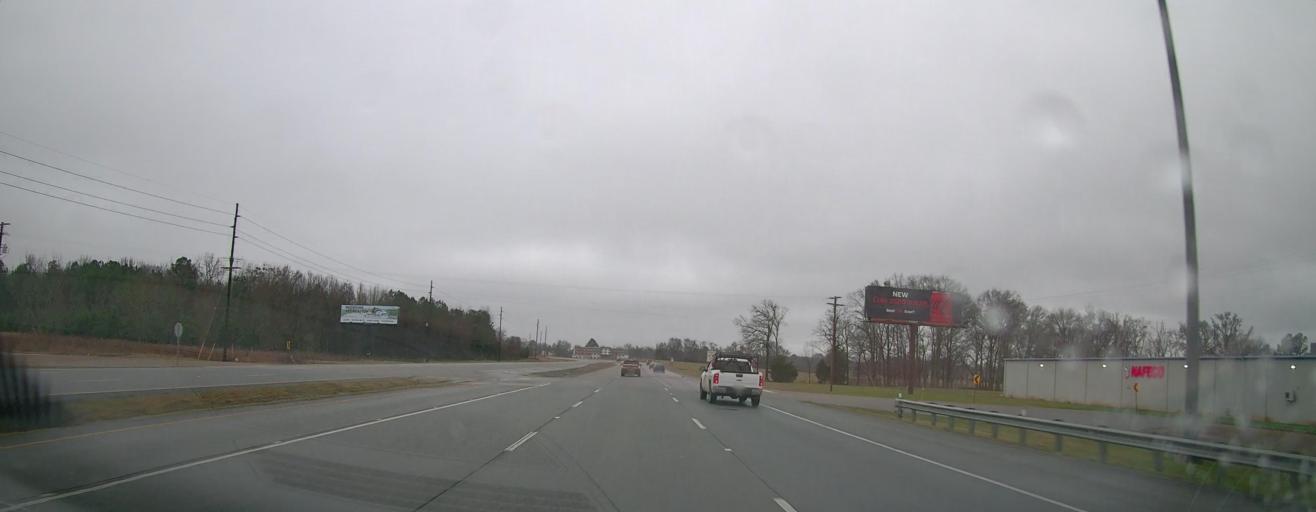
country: US
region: Alabama
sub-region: Morgan County
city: Decatur
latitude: 34.5989
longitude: -87.0315
